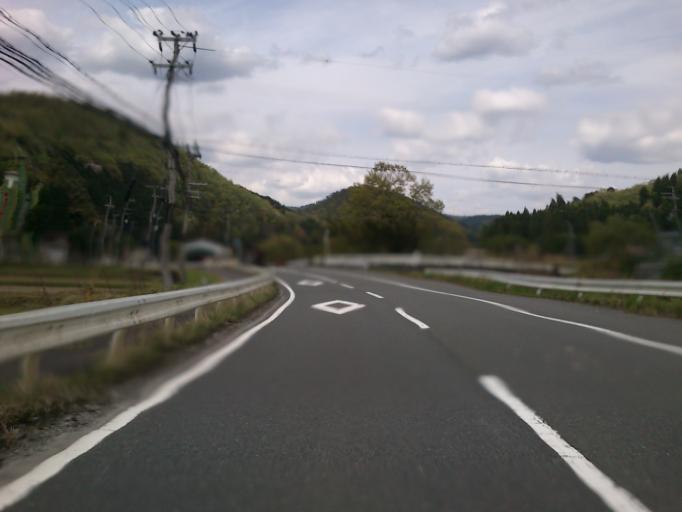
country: JP
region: Kyoto
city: Kameoka
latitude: 35.1779
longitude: 135.5126
